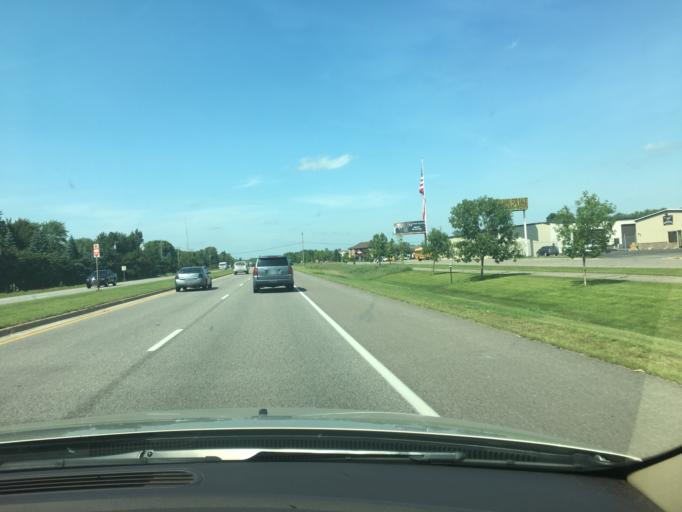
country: US
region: Minnesota
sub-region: Stearns County
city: Saint Cloud
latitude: 45.5256
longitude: -94.1624
